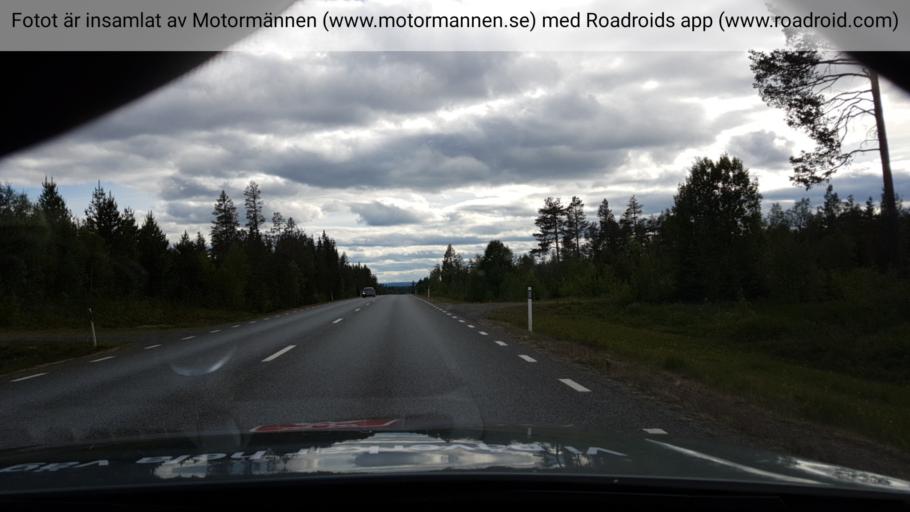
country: SE
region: Jaemtland
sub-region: Stroemsunds Kommun
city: Stroemsund
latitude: 63.7025
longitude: 15.4437
